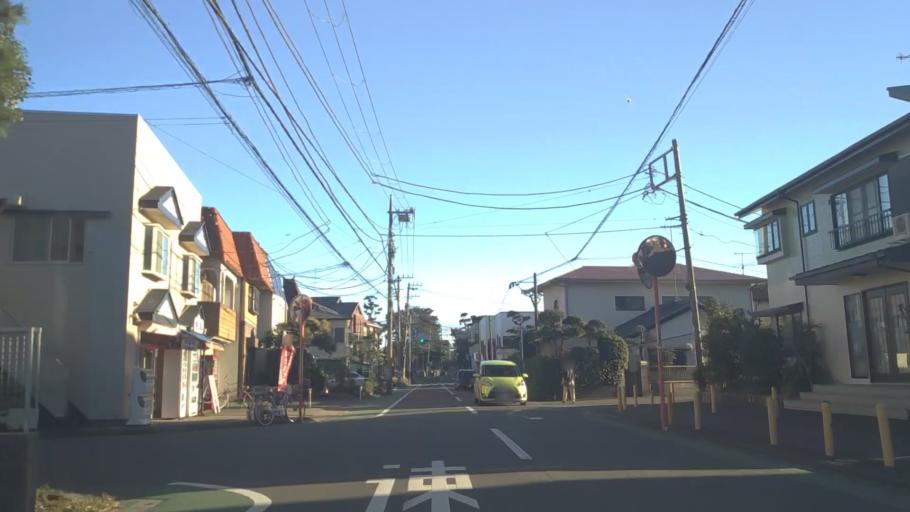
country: JP
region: Kanagawa
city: Chigasaki
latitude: 35.3233
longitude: 139.4152
